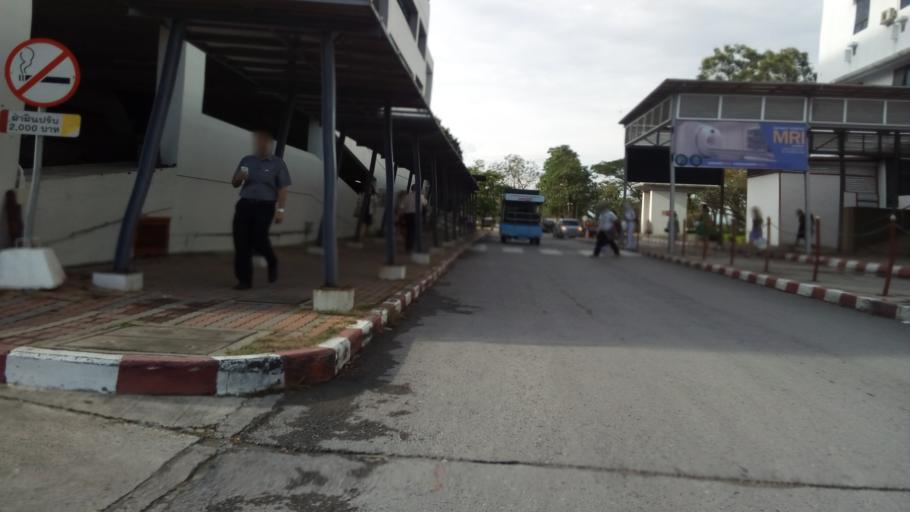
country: TH
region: Nakhon Nayok
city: Ongkharak
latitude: 14.1109
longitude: 100.9843
